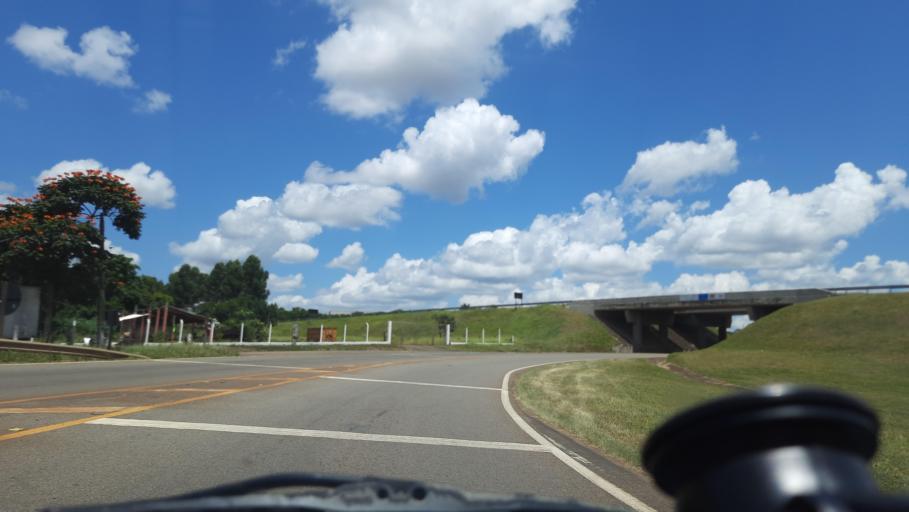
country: BR
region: Sao Paulo
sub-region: Casa Branca
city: Casa Branca
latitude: -21.7855
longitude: -47.0630
